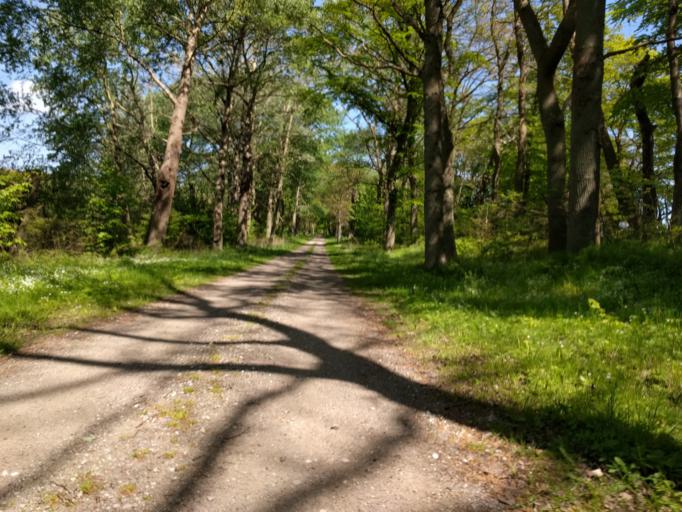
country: DK
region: Zealand
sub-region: Guldborgsund Kommune
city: Stubbekobing
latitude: 54.7842
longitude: 12.0746
